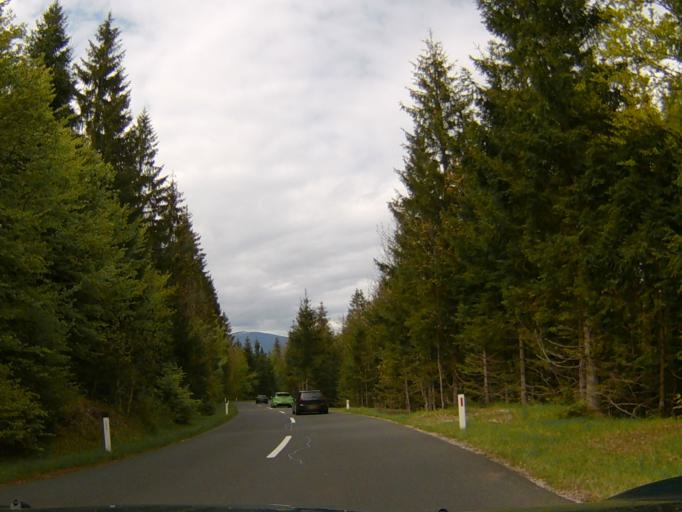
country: AT
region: Carinthia
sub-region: Villach Stadt
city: Villach
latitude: 46.5843
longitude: 13.7998
